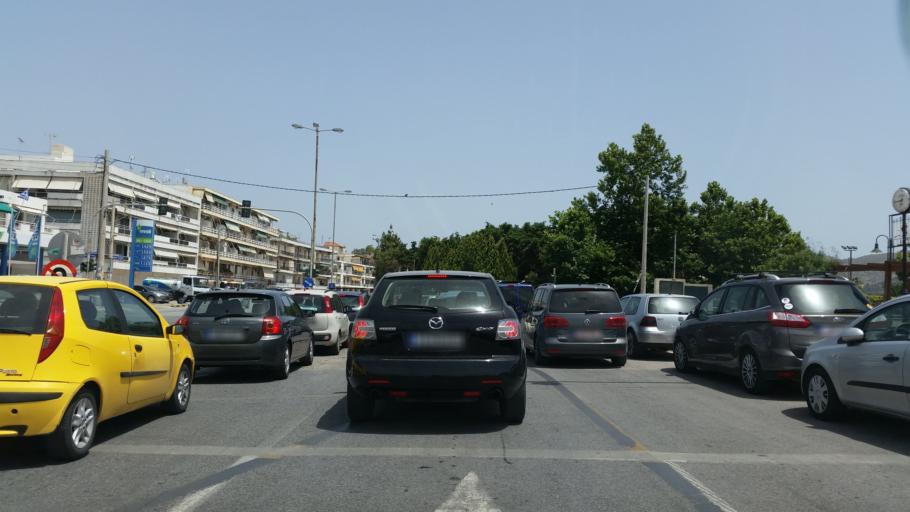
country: GR
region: Attica
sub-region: Nomarchia Anatolikis Attikis
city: Palaia Fokaia
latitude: 37.7246
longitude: 23.9429
